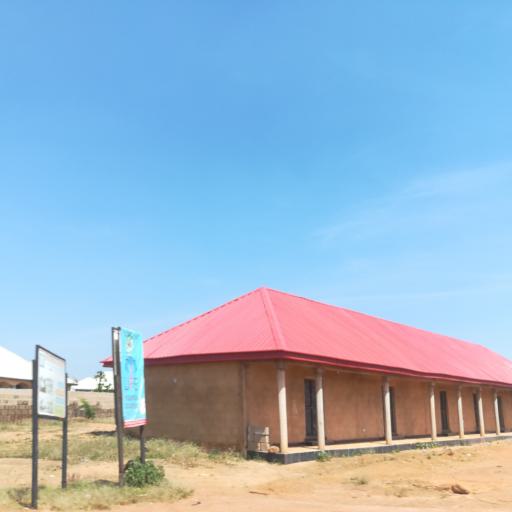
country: NG
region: Plateau
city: Jos
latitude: 9.8641
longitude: 8.9286
